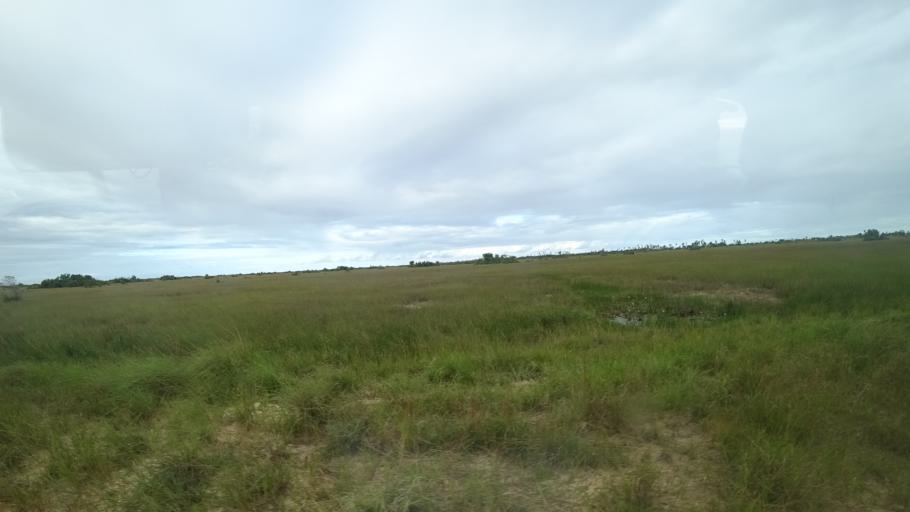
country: MZ
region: Sofala
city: Beira
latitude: -19.7066
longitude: 35.0181
